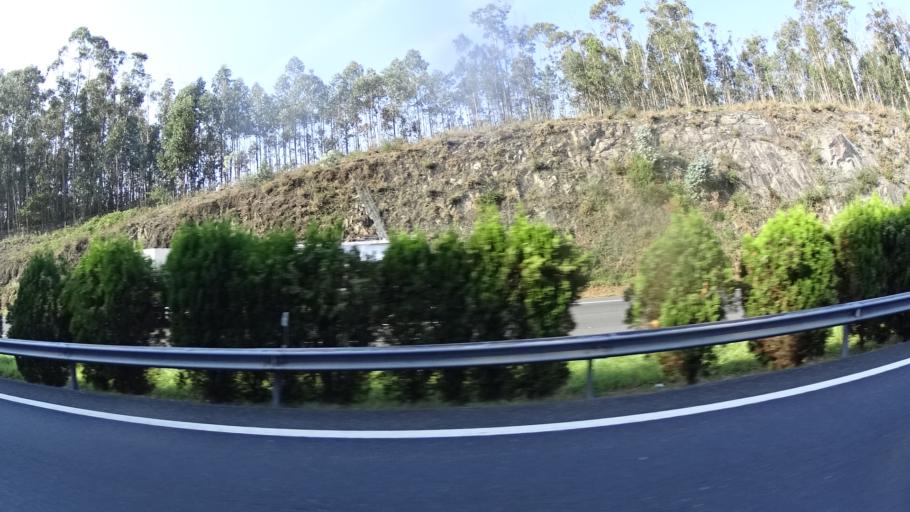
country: ES
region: Galicia
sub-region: Provincia da Coruna
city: Irixoa
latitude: 43.2383
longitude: -8.0908
